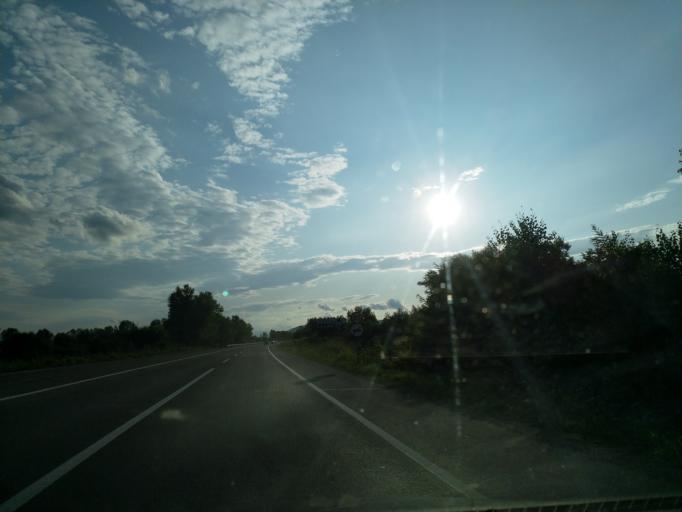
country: RS
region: Central Serbia
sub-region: Rasinski Okrug
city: Krusevac
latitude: 43.6098
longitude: 21.3393
